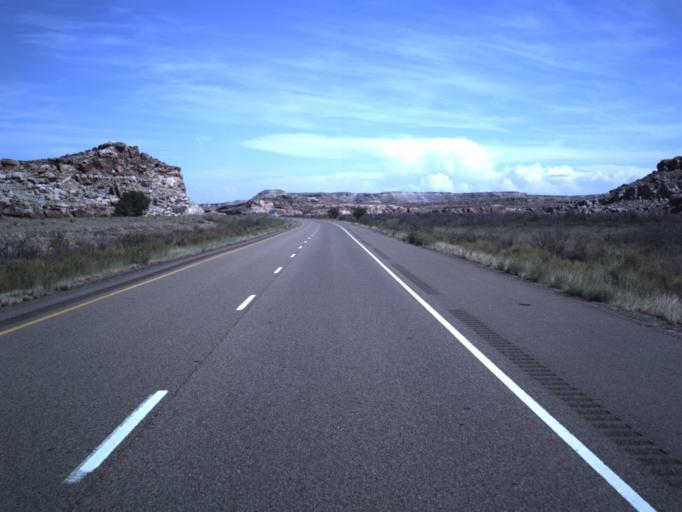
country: US
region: Utah
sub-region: Carbon County
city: East Carbon City
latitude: 38.9223
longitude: -110.4004
